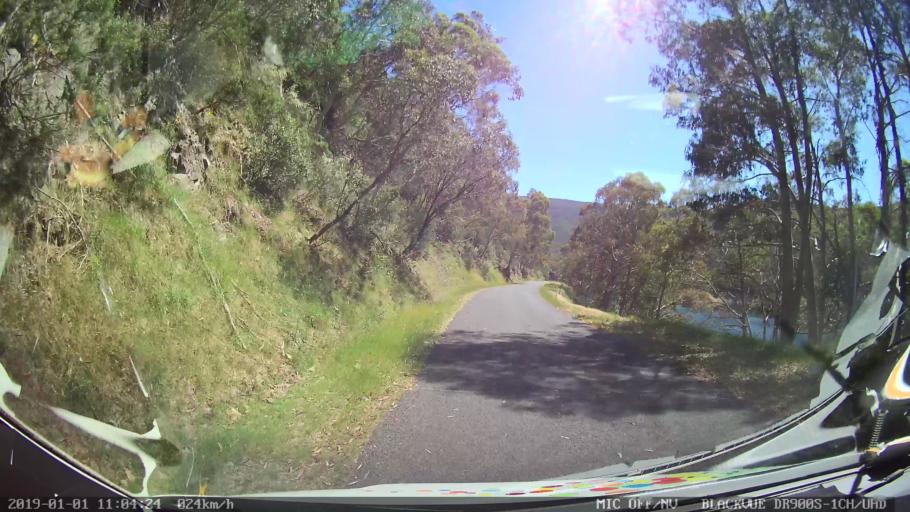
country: AU
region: New South Wales
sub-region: Snowy River
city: Jindabyne
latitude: -35.9703
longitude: 148.3884
